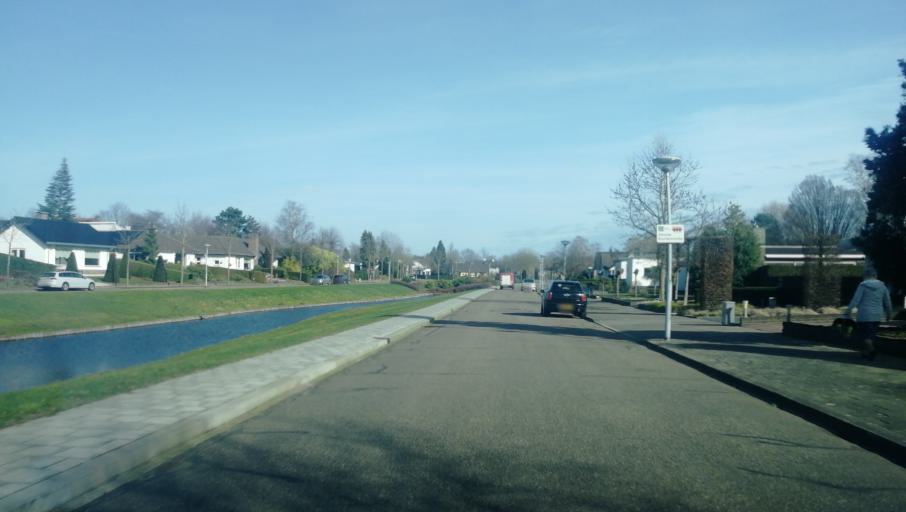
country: NL
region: Limburg
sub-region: Gemeente Venlo
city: Venlo
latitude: 51.3737
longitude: 6.1844
